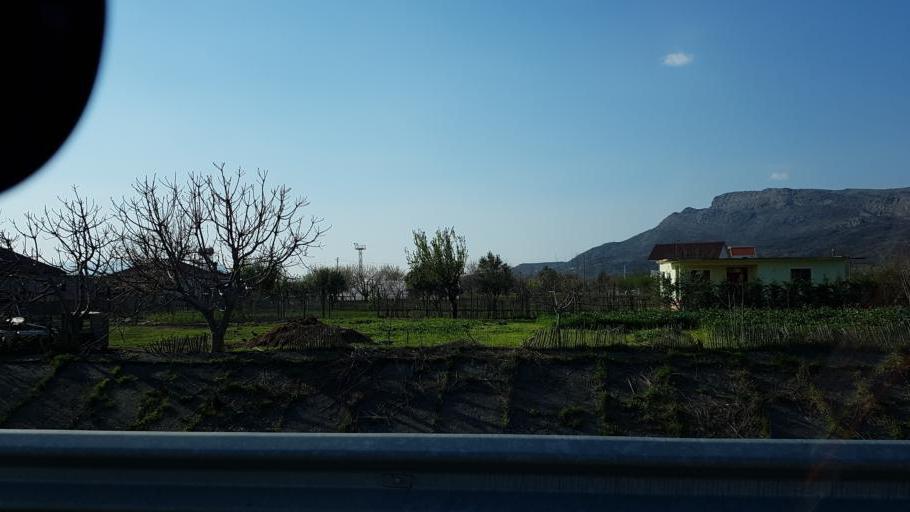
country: AL
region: Shkoder
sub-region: Rrethi i Shkodres
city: Vau i Dejes
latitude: 41.9947
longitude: 19.6106
